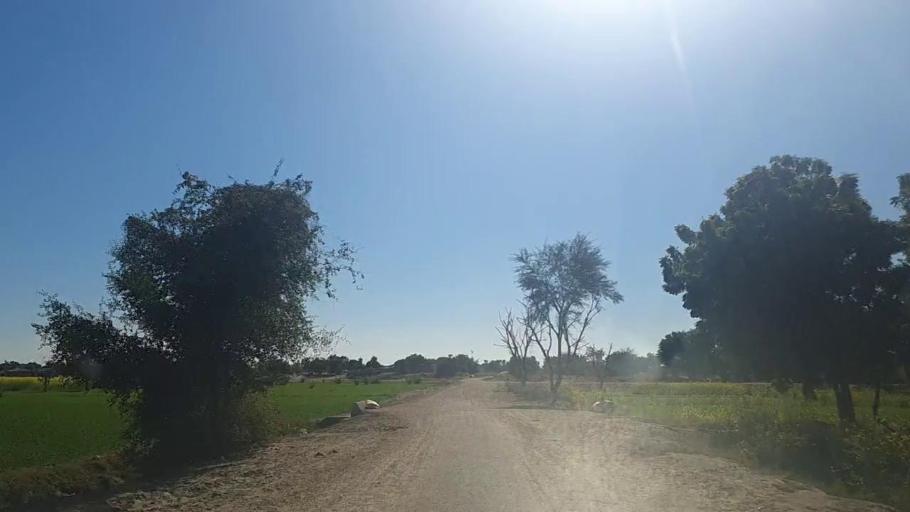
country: PK
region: Sindh
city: Sanghar
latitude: 26.1942
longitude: 68.9105
